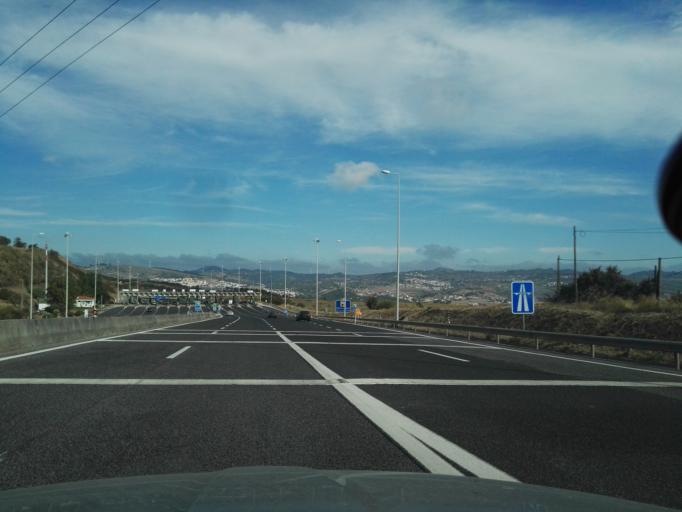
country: PT
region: Lisbon
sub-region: Odivelas
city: Ramada
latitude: 38.8174
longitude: -9.1855
